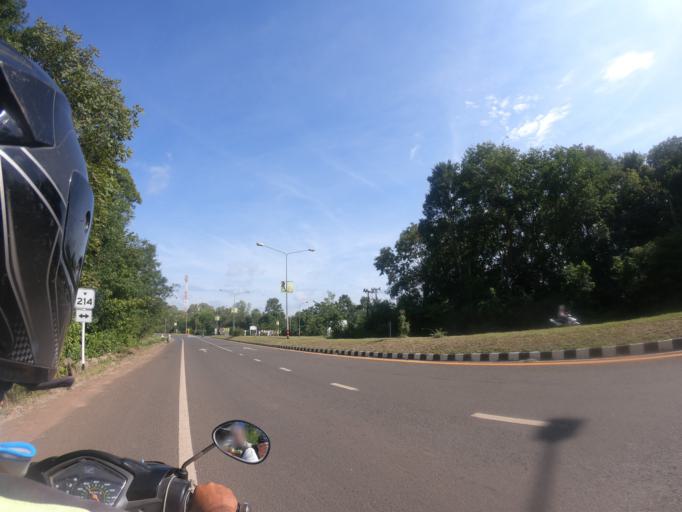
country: TH
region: Surin
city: Kap Choeng
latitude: 14.4505
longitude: 103.6992
